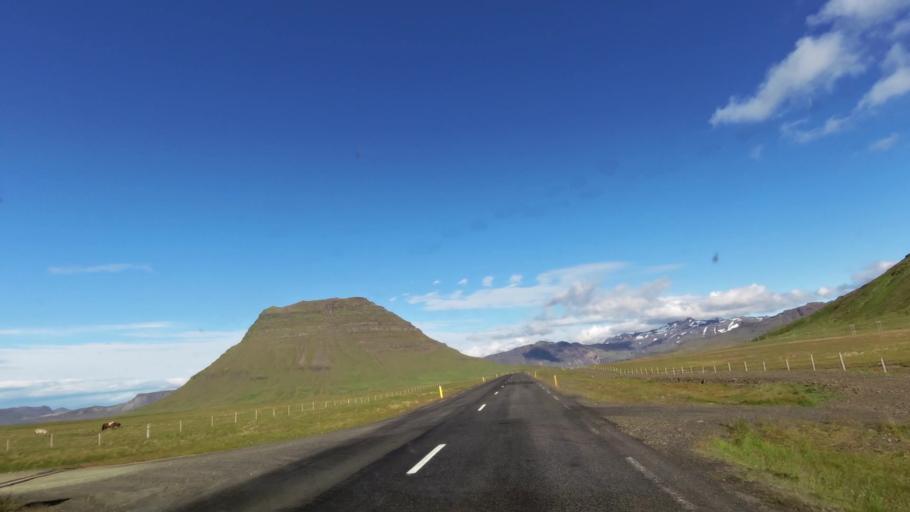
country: IS
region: West
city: Olafsvik
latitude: 64.9405
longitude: -23.3689
